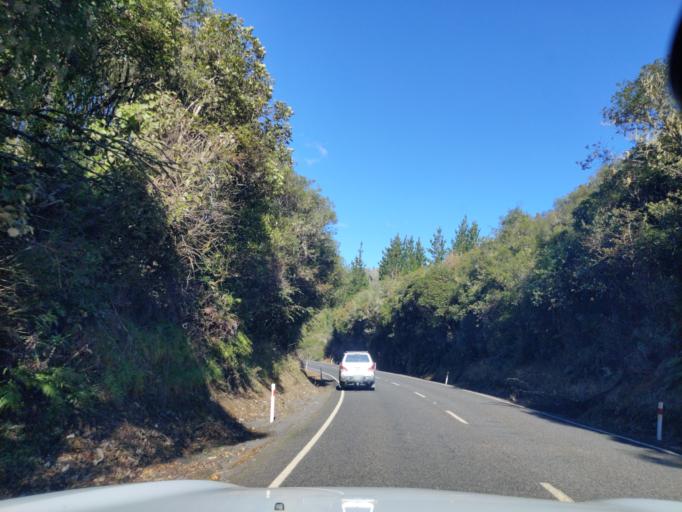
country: NZ
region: Waikato
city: Turangi
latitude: -38.7532
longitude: 175.6752
